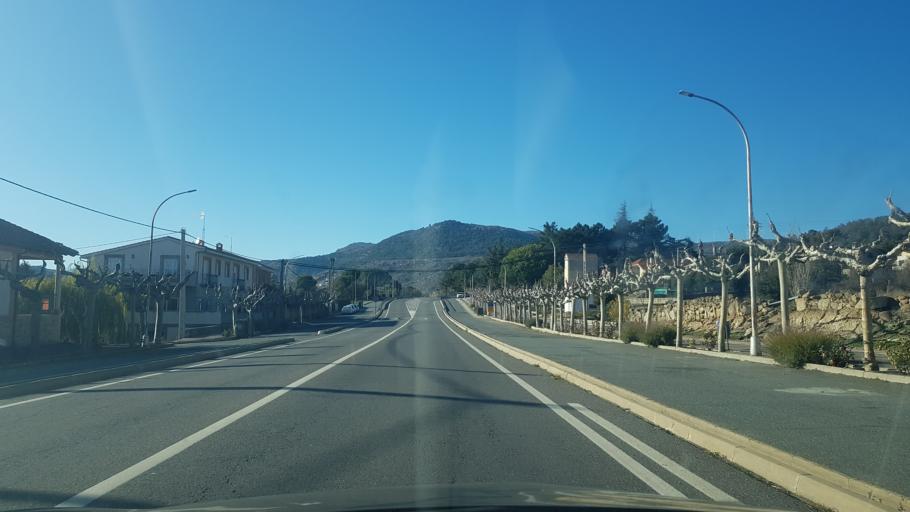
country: ES
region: Castille and Leon
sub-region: Provincia de Avila
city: Barraco
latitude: 40.4787
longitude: -4.6498
